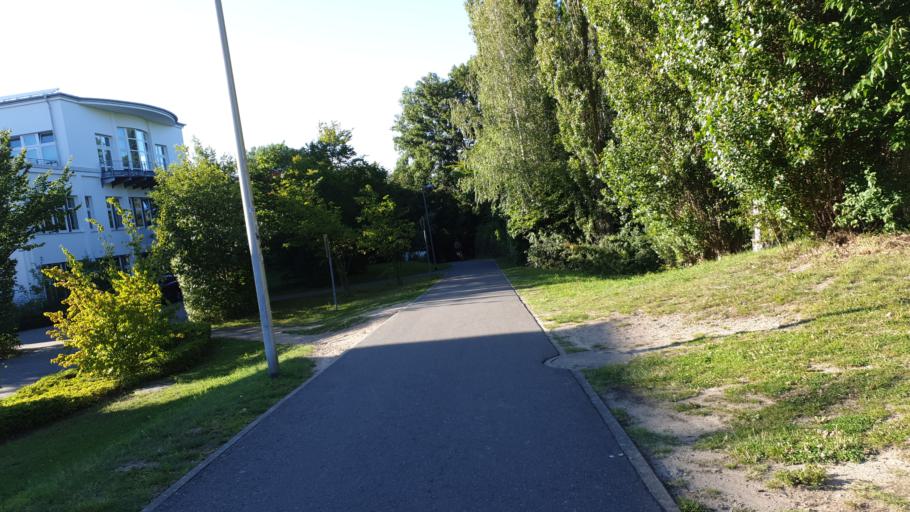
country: DE
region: Mecklenburg-Vorpommern
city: Stralsund
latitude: 54.3351
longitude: 13.0790
